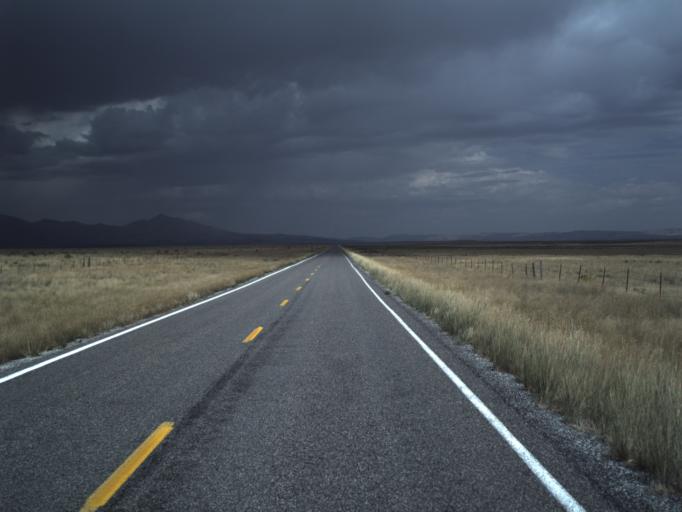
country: US
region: Idaho
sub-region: Oneida County
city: Malad City
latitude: 41.8867
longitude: -113.1142
